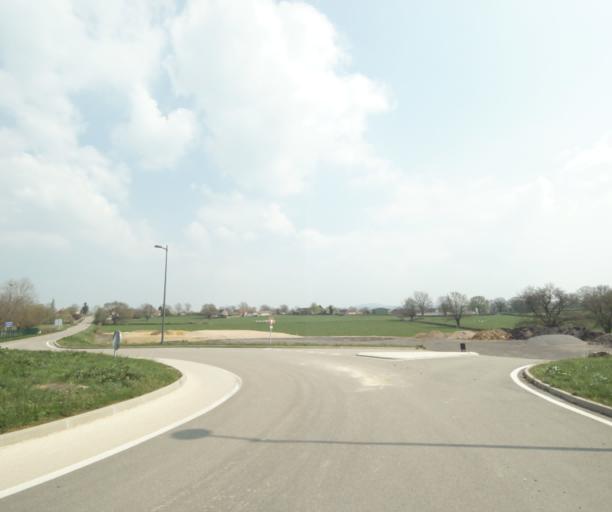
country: FR
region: Bourgogne
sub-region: Departement de Saone-et-Loire
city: Charolles
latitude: 46.4421
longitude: 4.3125
